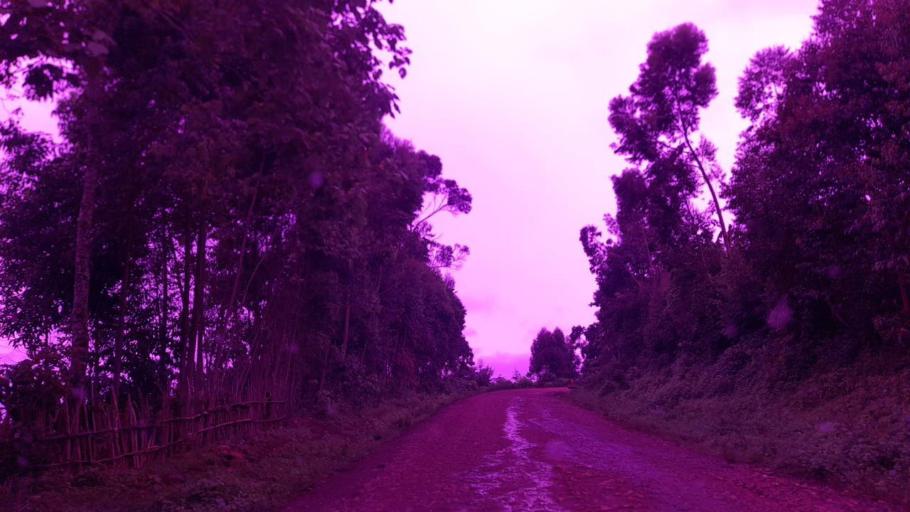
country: ET
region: Southern Nations, Nationalities, and People's Region
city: Tippi
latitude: 7.5801
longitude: 35.7750
